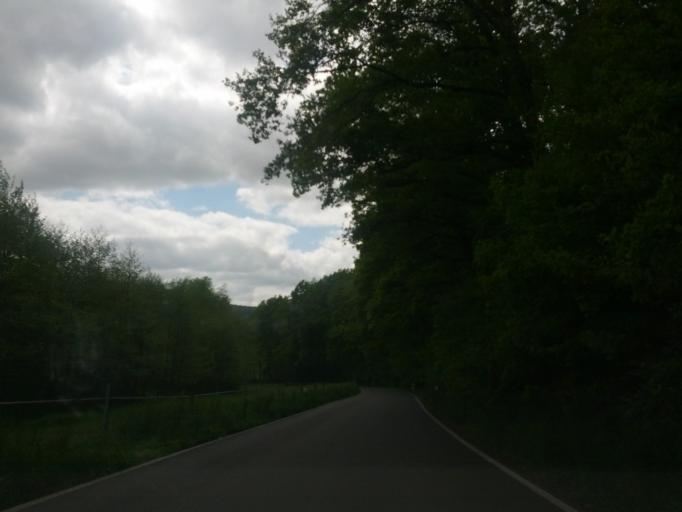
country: DE
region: Saxony
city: Kreischa
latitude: 50.9368
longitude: 13.7835
